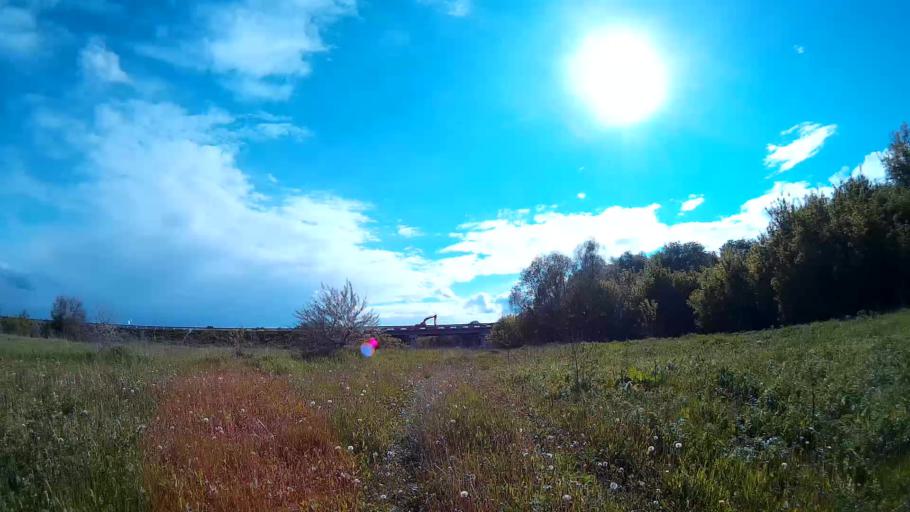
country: RU
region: Ulyanovsk
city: Novoul'yanovsk
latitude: 54.2245
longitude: 48.2648
